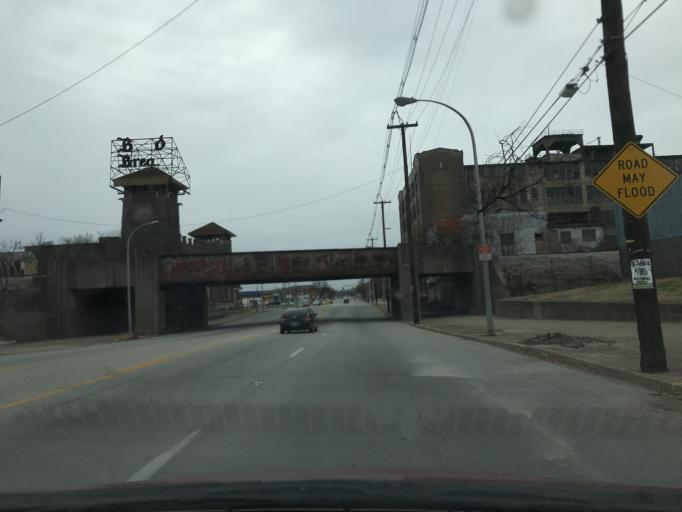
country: US
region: Kentucky
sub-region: Jefferson County
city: Louisville
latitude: 38.2480
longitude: -85.7740
